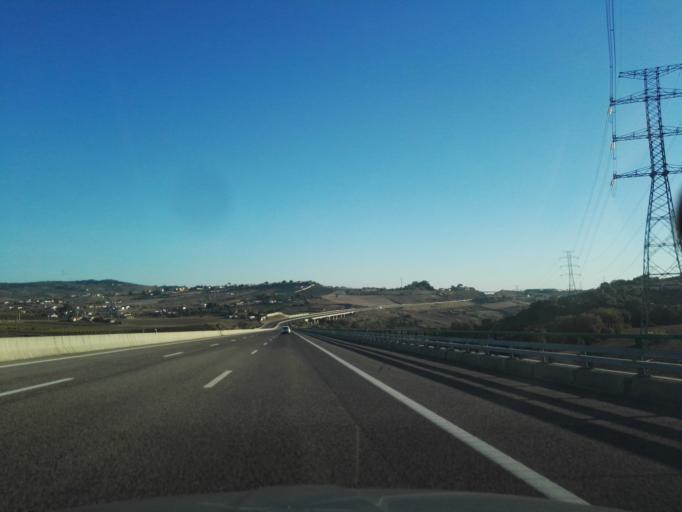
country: PT
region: Lisbon
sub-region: Arruda Dos Vinhos
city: Arruda dos Vinhos
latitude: 38.9805
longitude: -9.0561
